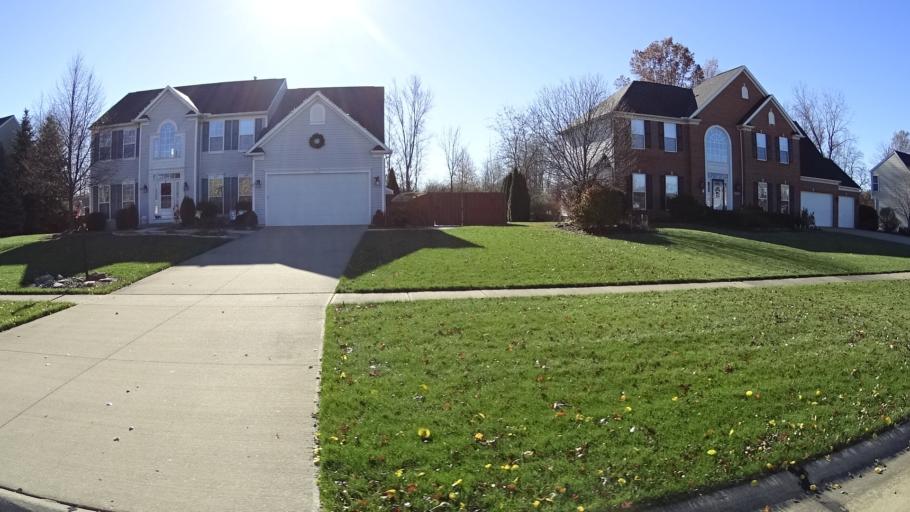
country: US
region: Ohio
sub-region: Lorain County
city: Avon
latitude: 41.4193
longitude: -82.0538
